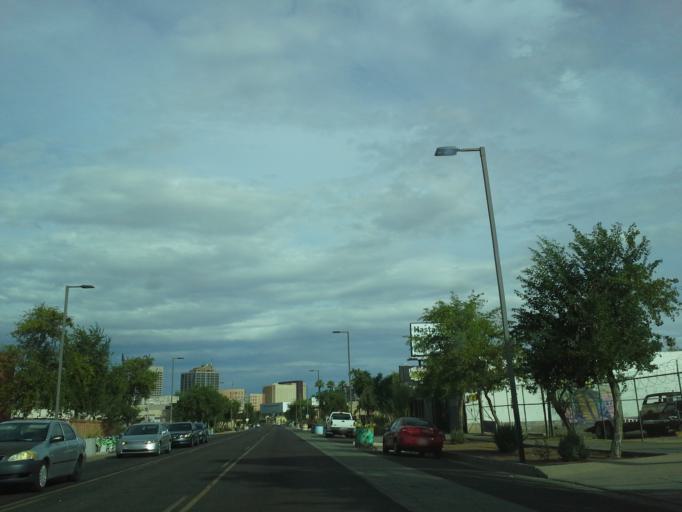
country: US
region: Arizona
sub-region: Maricopa County
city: Phoenix
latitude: 33.4549
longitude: -112.0868
